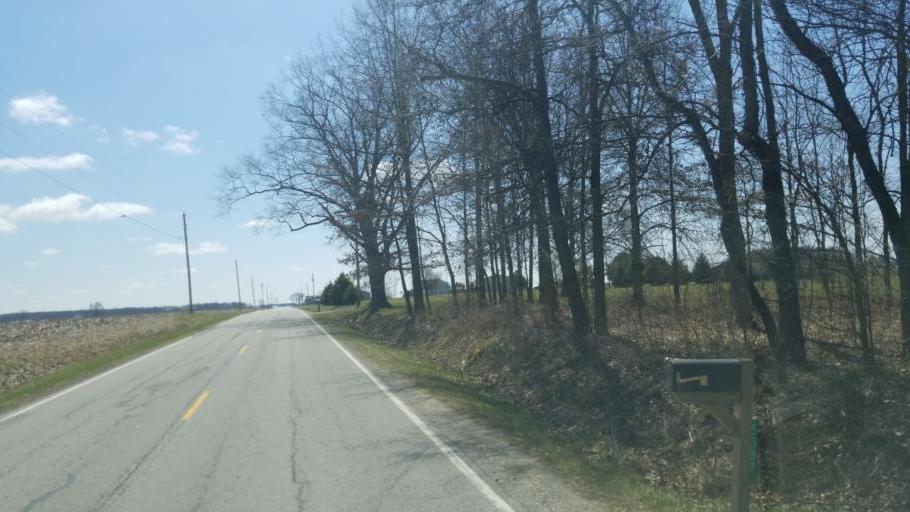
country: US
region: Ohio
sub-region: Wyandot County
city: Upper Sandusky
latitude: 40.6945
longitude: -83.2425
